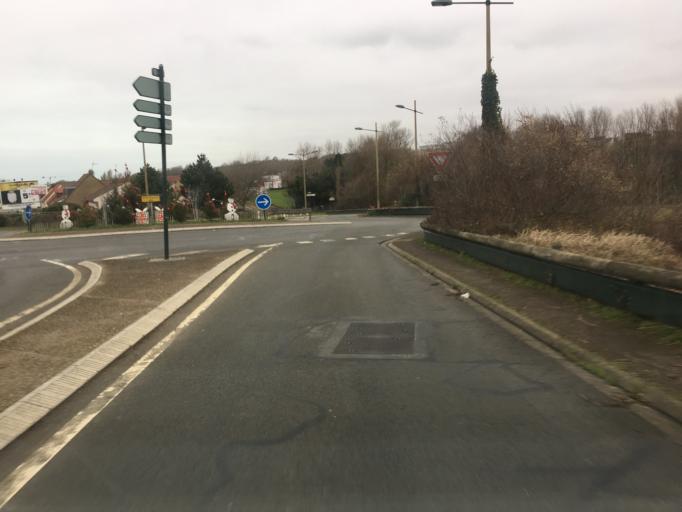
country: FR
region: Nord-Pas-de-Calais
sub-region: Departement du Pas-de-Calais
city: Le Portel
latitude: 50.6943
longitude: 1.5787
